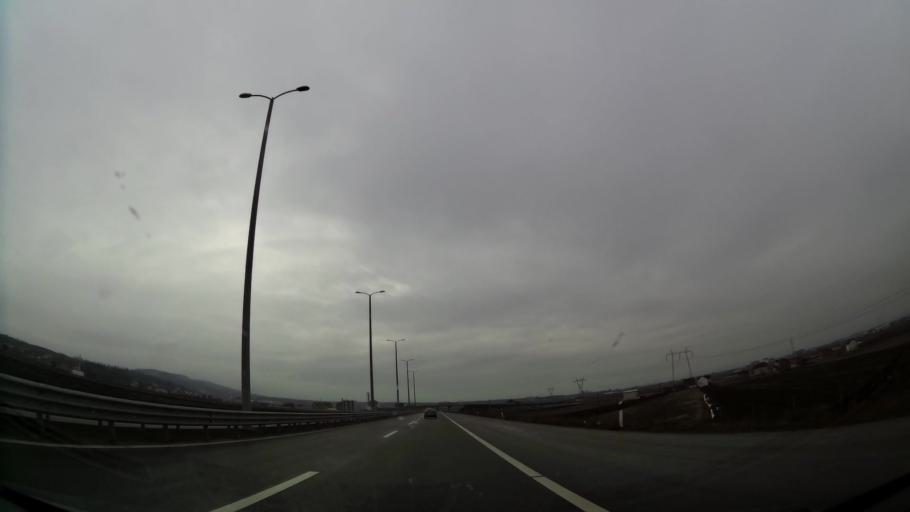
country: XK
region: Pristina
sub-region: Lipjan
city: Lipljan
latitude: 42.4922
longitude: 21.1886
